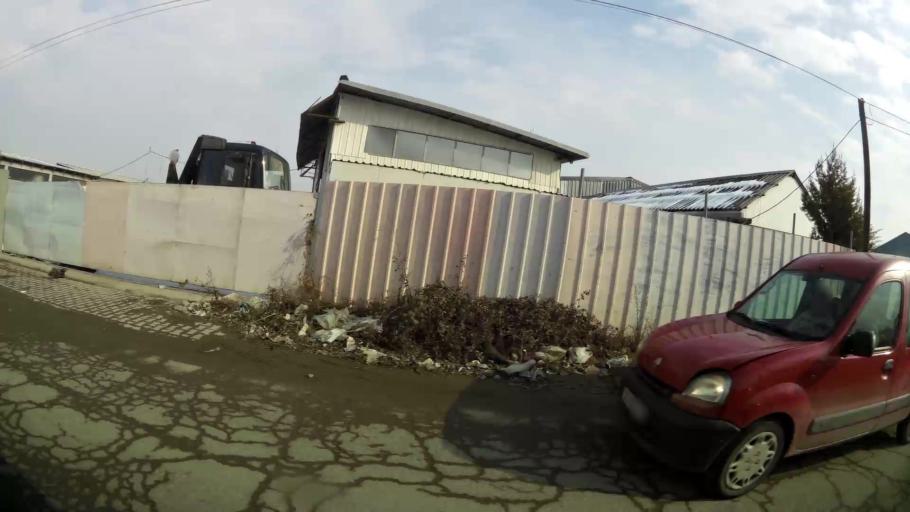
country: MK
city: Krushopek
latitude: 42.0165
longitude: 21.3683
